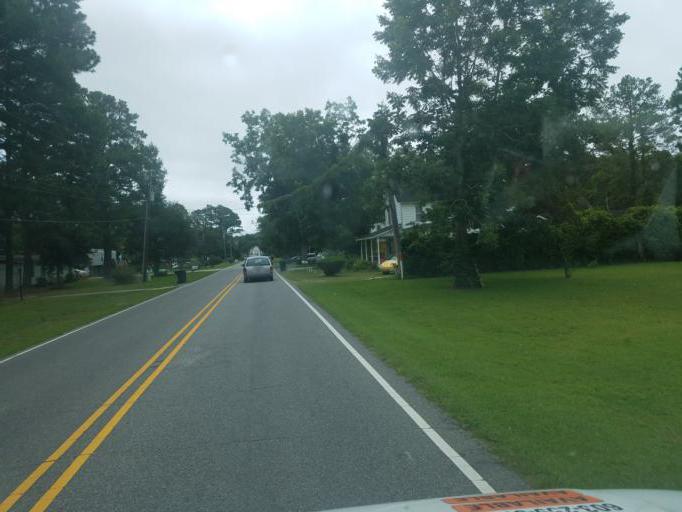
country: US
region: North Carolina
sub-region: Dare County
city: Wanchese
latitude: 35.8474
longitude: -75.6394
